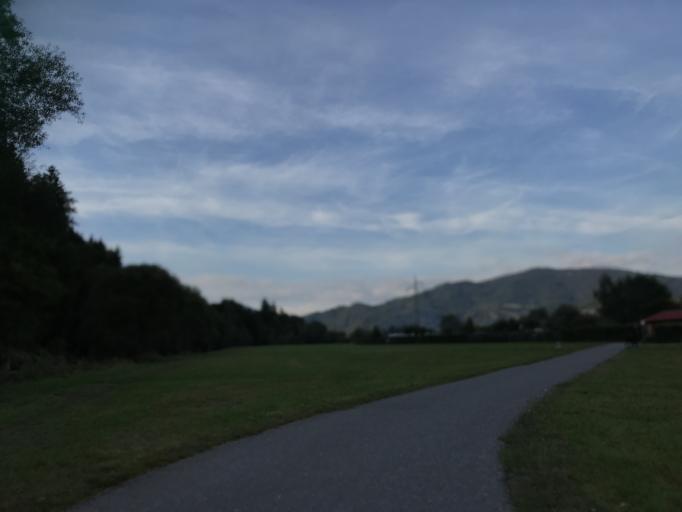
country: DE
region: Baden-Wuerttemberg
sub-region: Freiburg Region
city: Schopfheim
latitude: 47.6586
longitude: 7.8288
